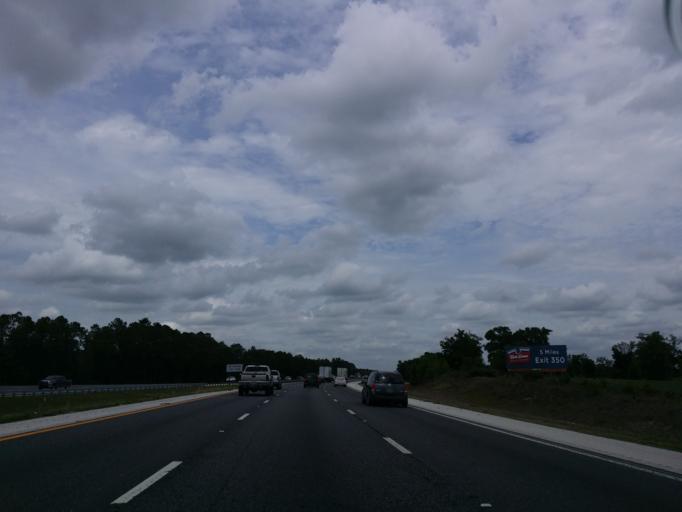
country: US
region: Florida
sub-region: Marion County
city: Ocala
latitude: 29.0791
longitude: -82.1847
